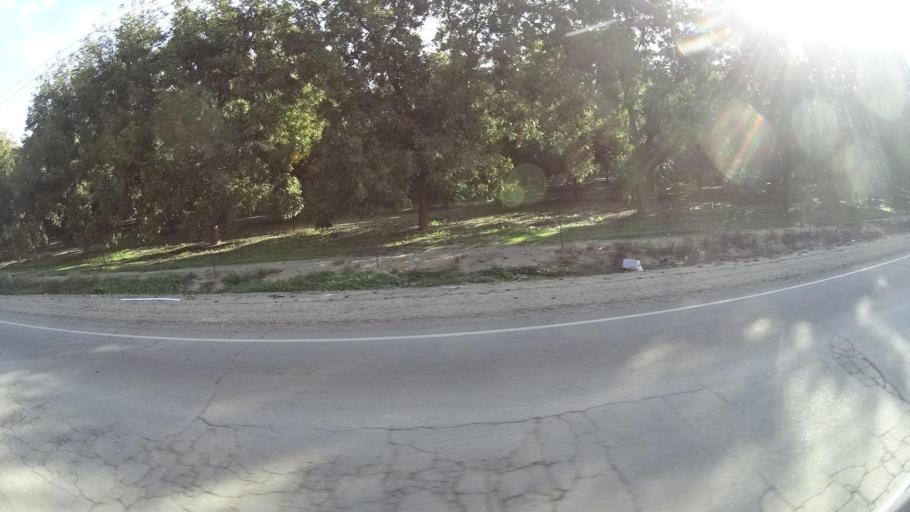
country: US
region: California
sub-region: Kern County
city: McFarland
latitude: 35.6269
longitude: -119.2044
